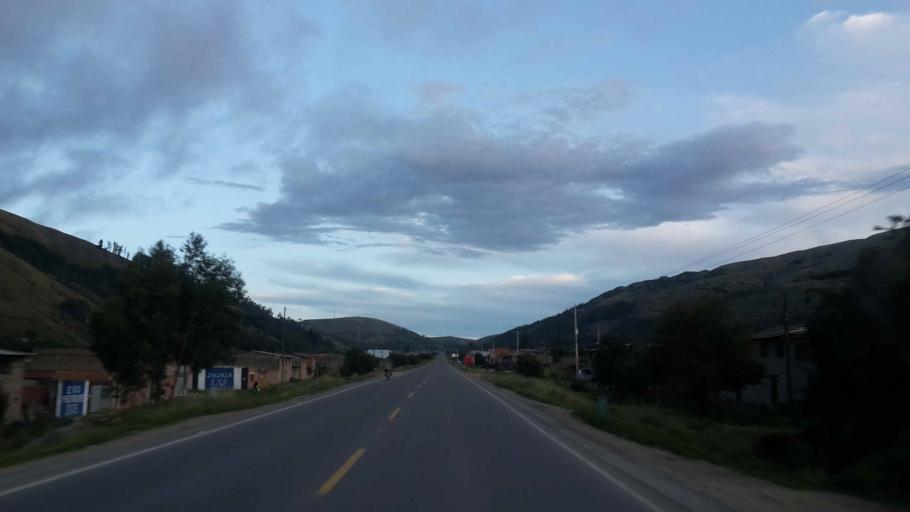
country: BO
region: Cochabamba
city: Colomi
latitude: -17.3441
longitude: -65.8594
